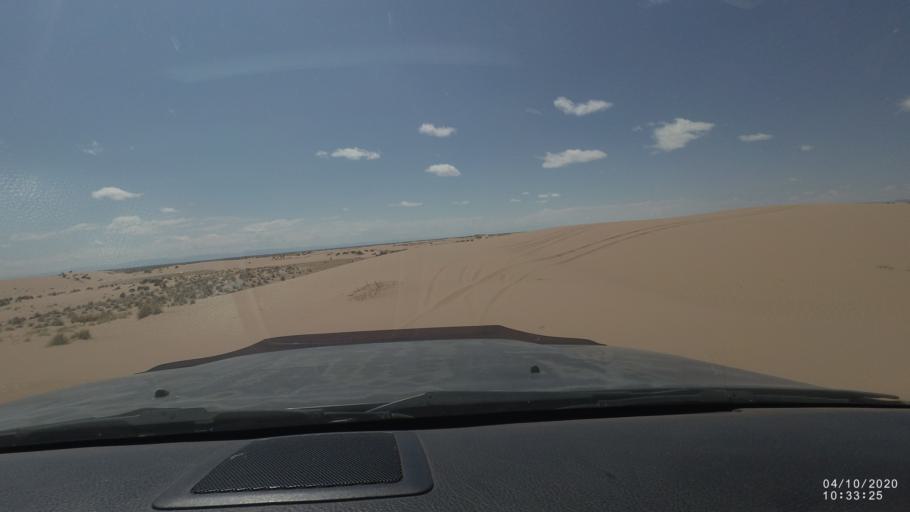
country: BO
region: Oruro
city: Poopo
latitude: -18.7045
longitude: -67.4797
